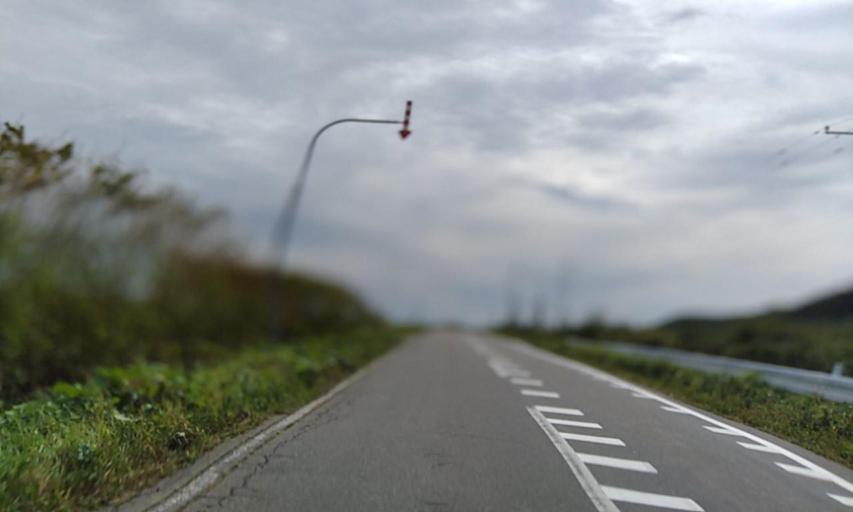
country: JP
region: Hokkaido
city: Kushiro
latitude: 42.7923
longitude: 143.7976
